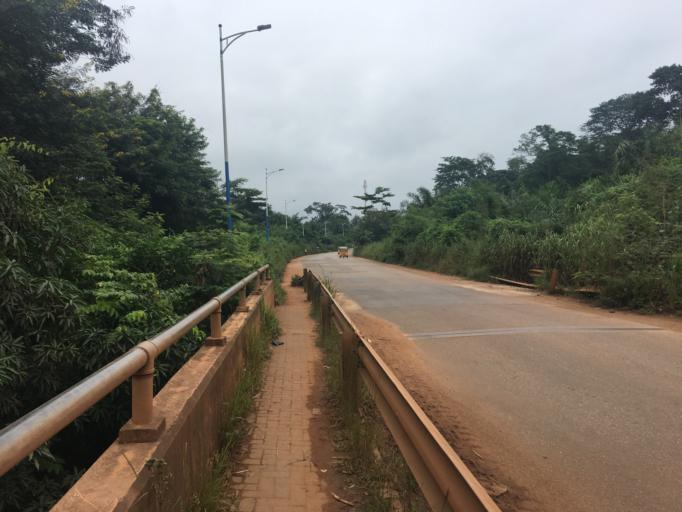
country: GH
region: Western
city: Bibiani
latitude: 6.8081
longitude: -2.5096
